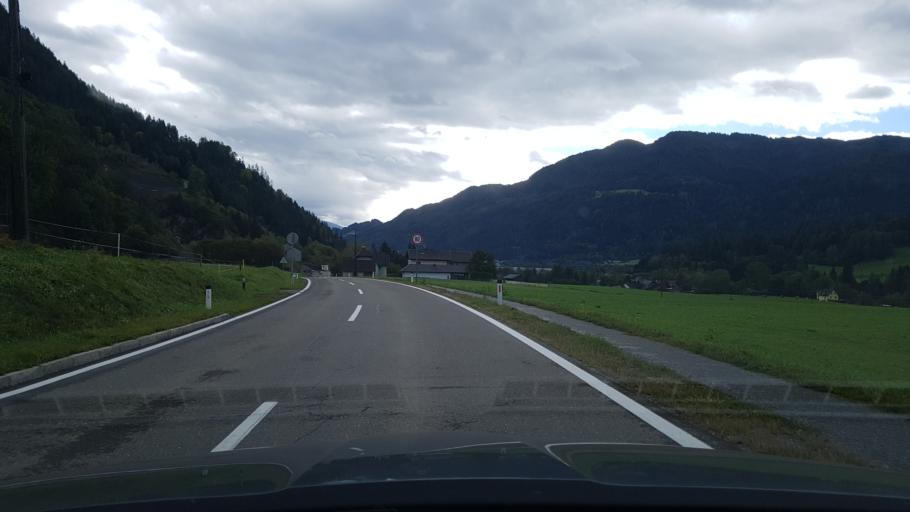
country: AT
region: Styria
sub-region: Politischer Bezirk Murau
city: Oberwolz Stadt
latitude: 47.1491
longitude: 14.2736
